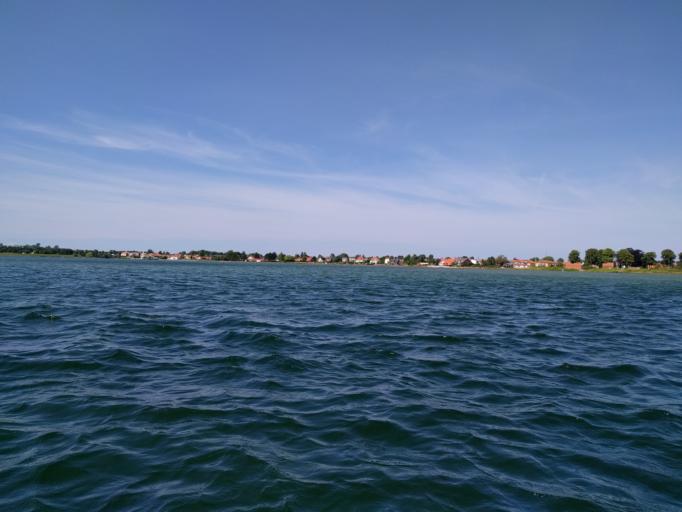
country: DK
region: South Denmark
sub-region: Kerteminde Kommune
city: Kerteminde
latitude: 55.4442
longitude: 10.6479
